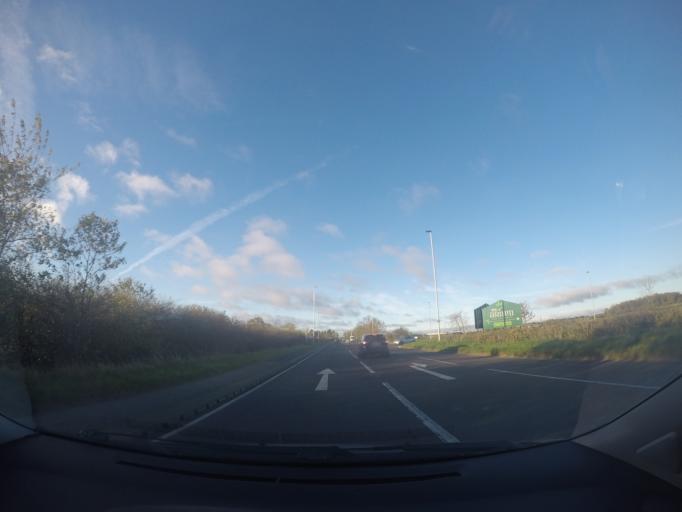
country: GB
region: England
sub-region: City and Borough of Leeds
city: Scholes
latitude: 53.8337
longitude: -1.4375
